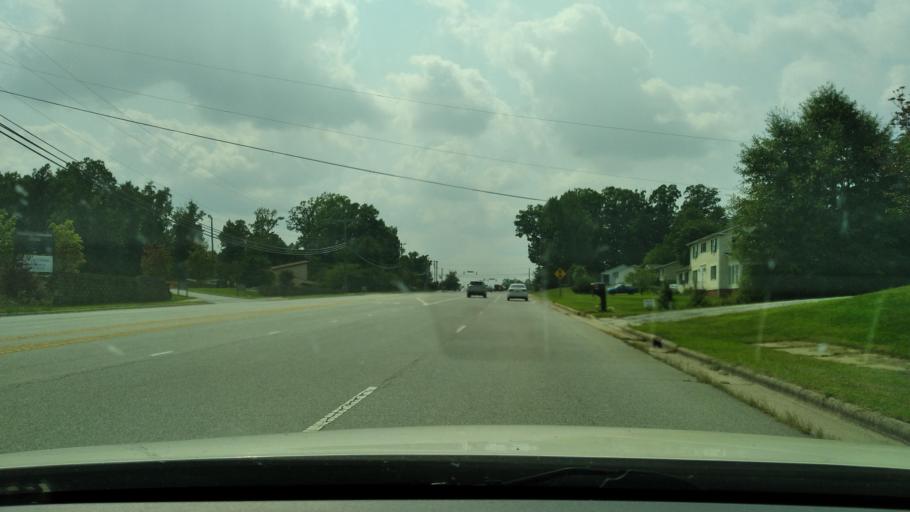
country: US
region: North Carolina
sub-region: Guilford County
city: Jamestown
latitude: 36.0392
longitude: -79.9166
